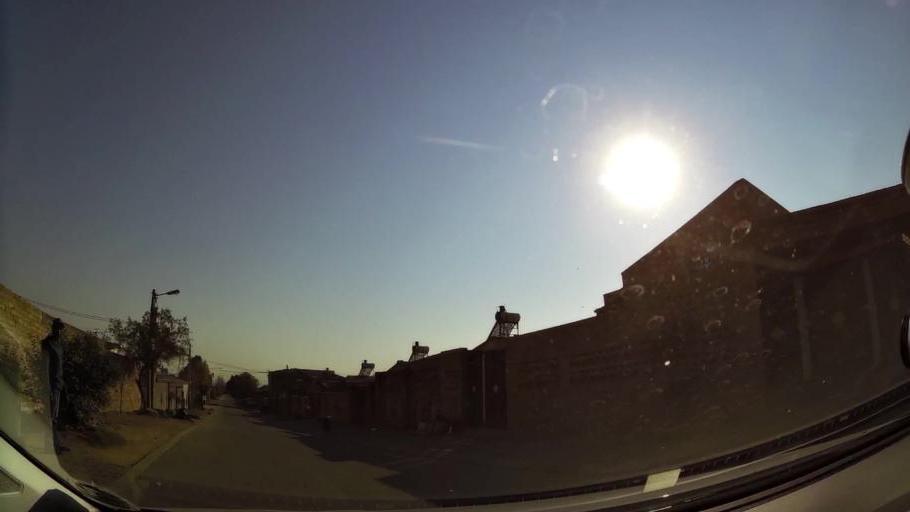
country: ZA
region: Gauteng
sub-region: City of Johannesburg Metropolitan Municipality
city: Modderfontein
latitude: -26.0910
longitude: 28.1152
